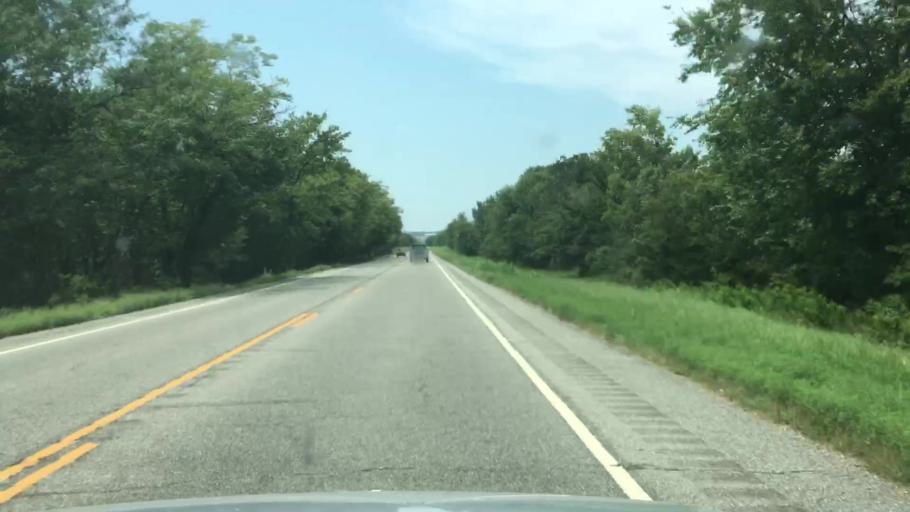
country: US
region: Oklahoma
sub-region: Muskogee County
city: Fort Gibson
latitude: 35.9370
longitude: -95.2007
